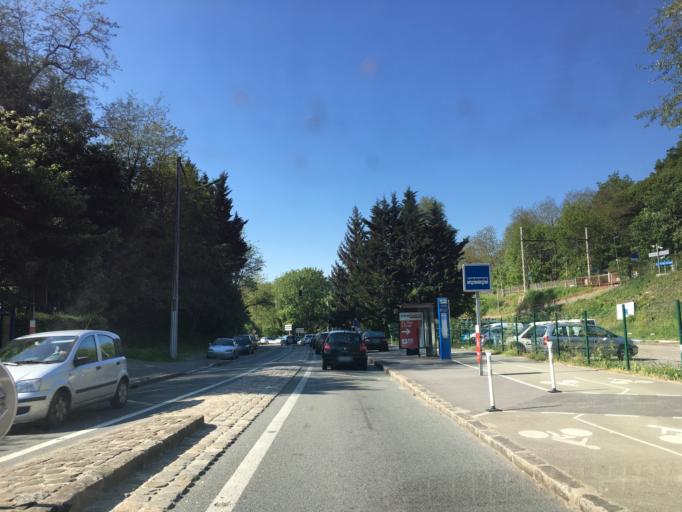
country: FR
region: Ile-de-France
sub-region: Departement des Yvelines
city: Les Loges-en-Josas
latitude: 48.7720
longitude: 2.1479
